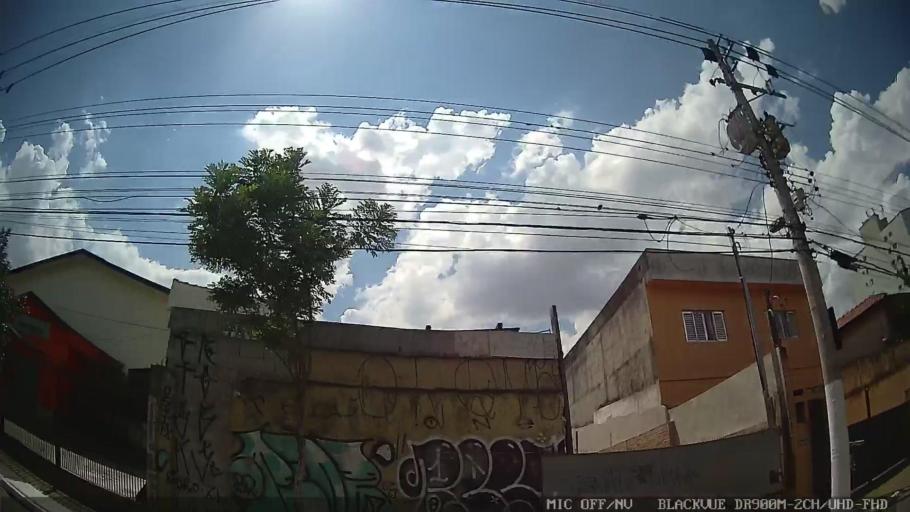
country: BR
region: Sao Paulo
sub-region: Ferraz De Vasconcelos
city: Ferraz de Vasconcelos
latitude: -23.5540
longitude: -46.4667
